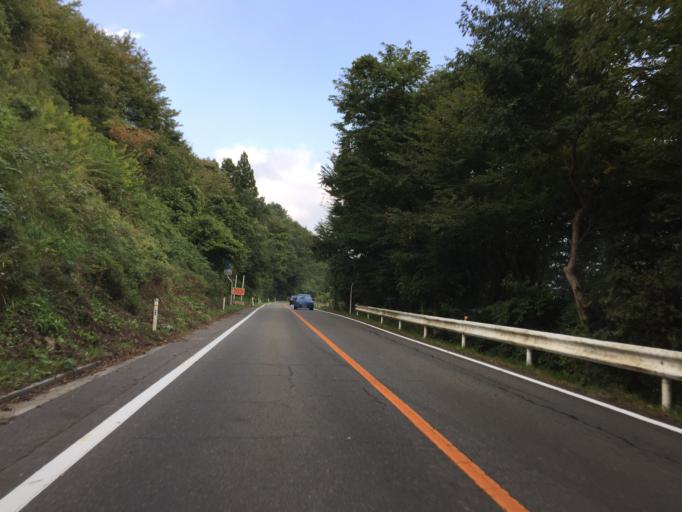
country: JP
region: Fukushima
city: Funehikimachi-funehiki
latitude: 37.5705
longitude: 140.7371
